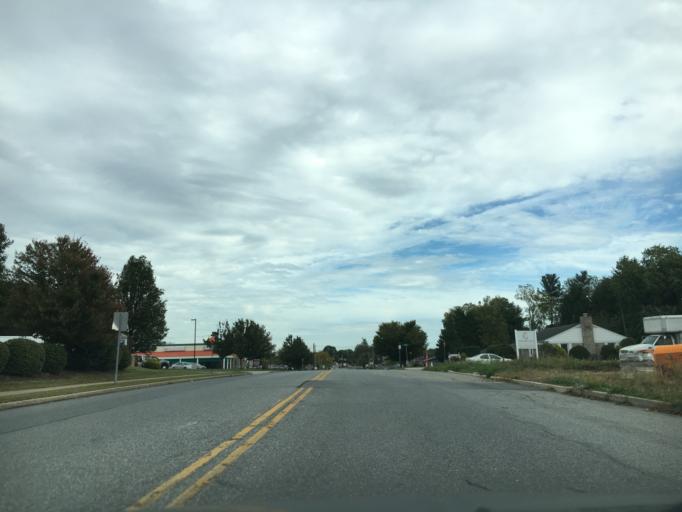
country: US
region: Pennsylvania
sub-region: York County
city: East York
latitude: 39.9721
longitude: -76.6826
